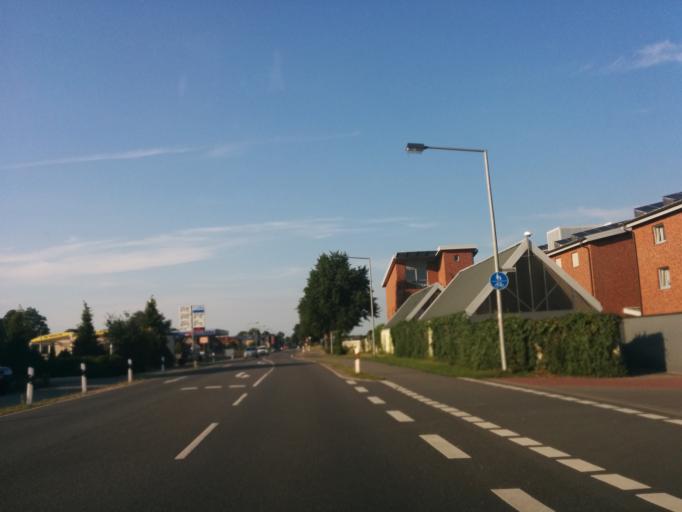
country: DE
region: North Rhine-Westphalia
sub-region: Regierungsbezirk Munster
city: Rheine
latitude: 52.2728
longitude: 7.4119
